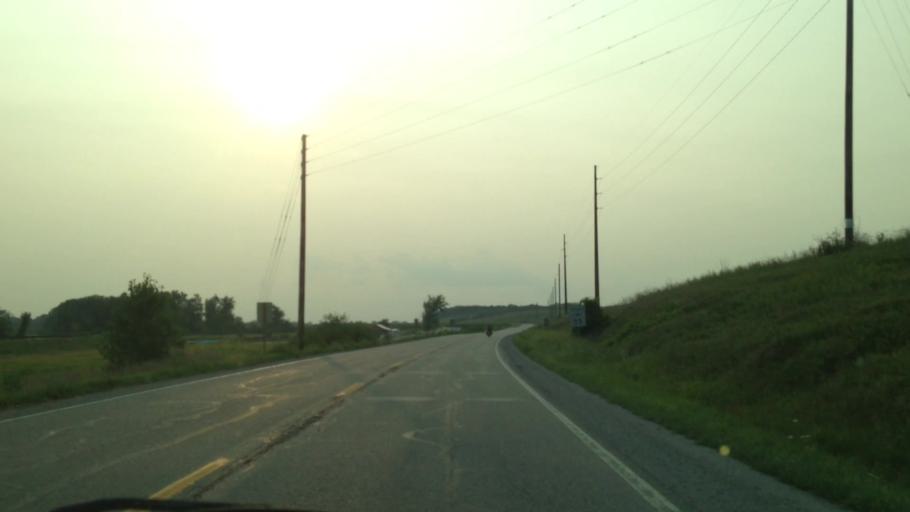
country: US
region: Iowa
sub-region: Benton County
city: Walford
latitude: 41.7950
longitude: -91.9082
